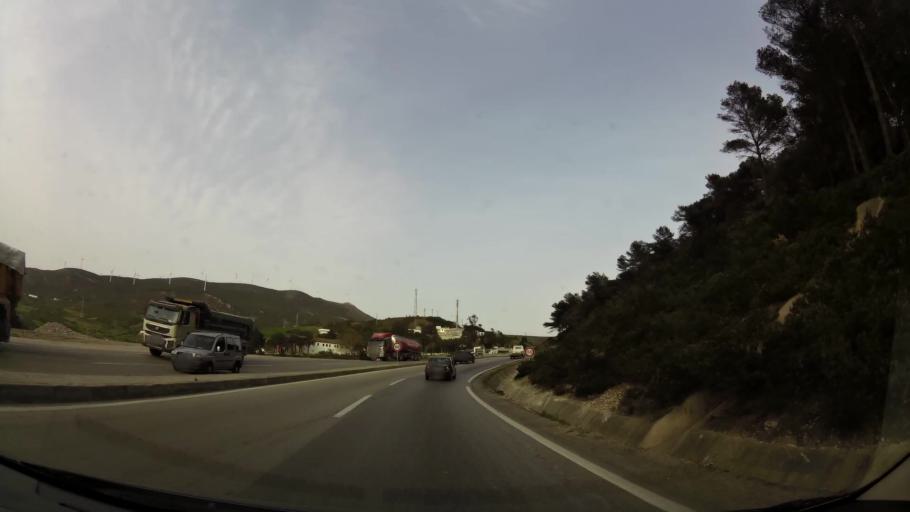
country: MA
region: Tanger-Tetouan
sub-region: Tetouan
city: Saddina
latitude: 35.5602
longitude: -5.5770
